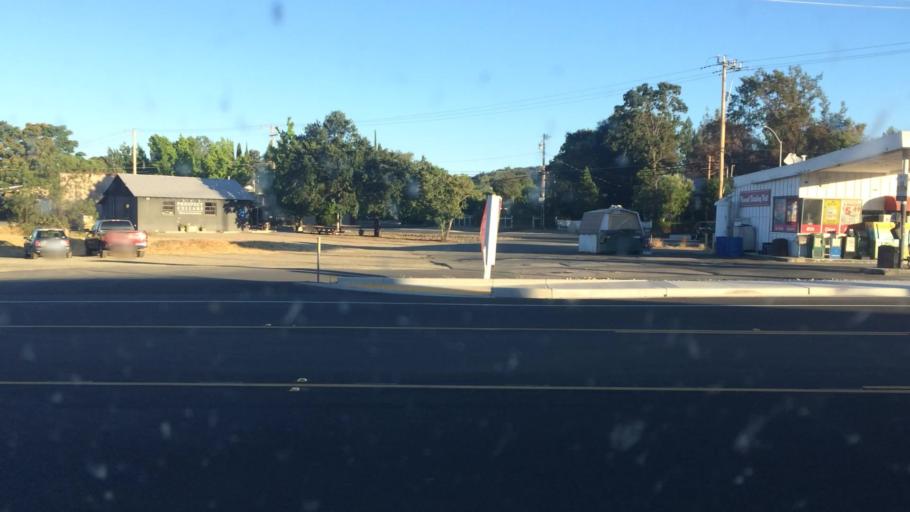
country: US
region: California
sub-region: Amador County
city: Plymouth
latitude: 38.4812
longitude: -120.8450
